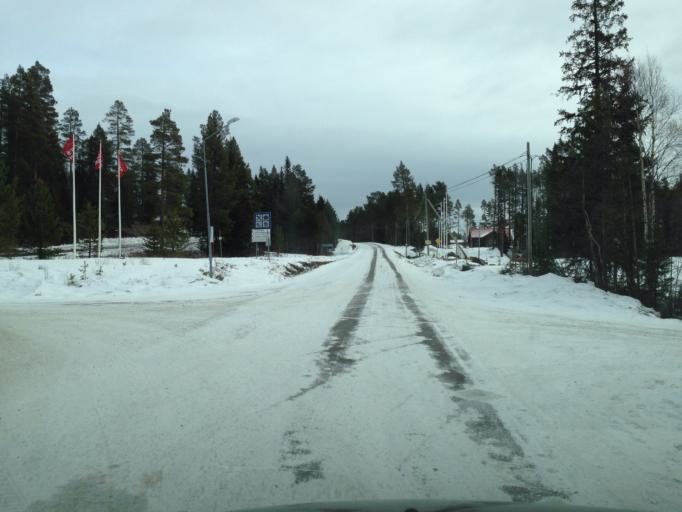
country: SE
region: Jaemtland
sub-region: Harjedalens Kommun
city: Sveg
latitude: 62.1112
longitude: 13.2876
